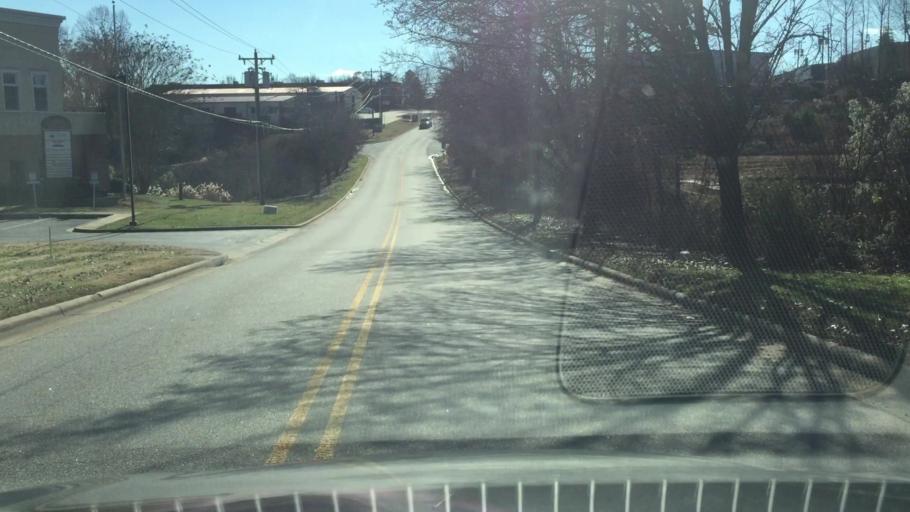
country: US
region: North Carolina
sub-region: Iredell County
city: Mooresville
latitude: 35.5930
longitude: -80.8627
